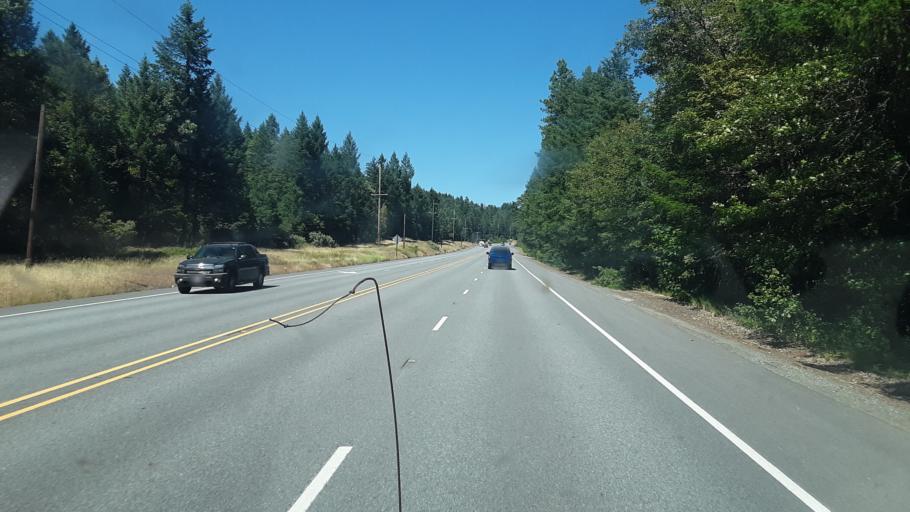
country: US
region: Oregon
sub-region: Josephine County
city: Cave Junction
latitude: 42.3250
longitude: -123.5954
